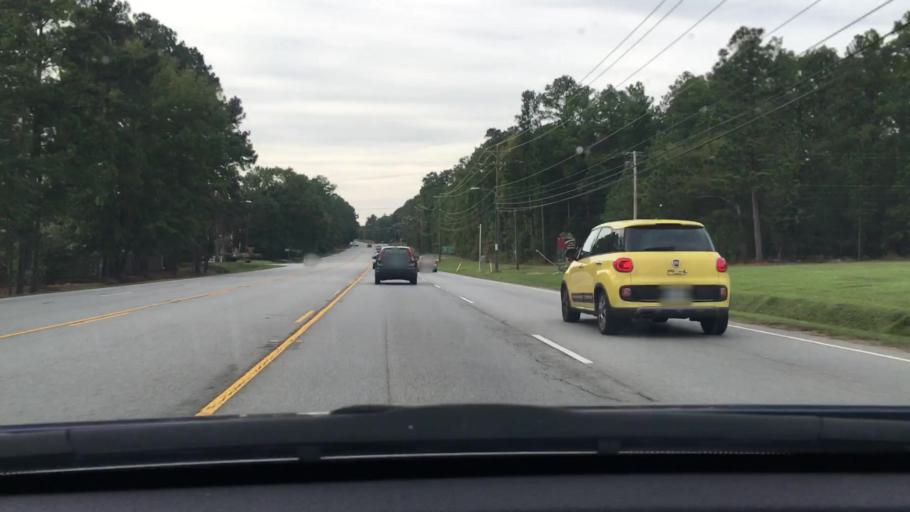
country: US
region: South Carolina
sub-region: Lexington County
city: Saint Andrews
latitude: 34.0791
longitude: -81.1296
